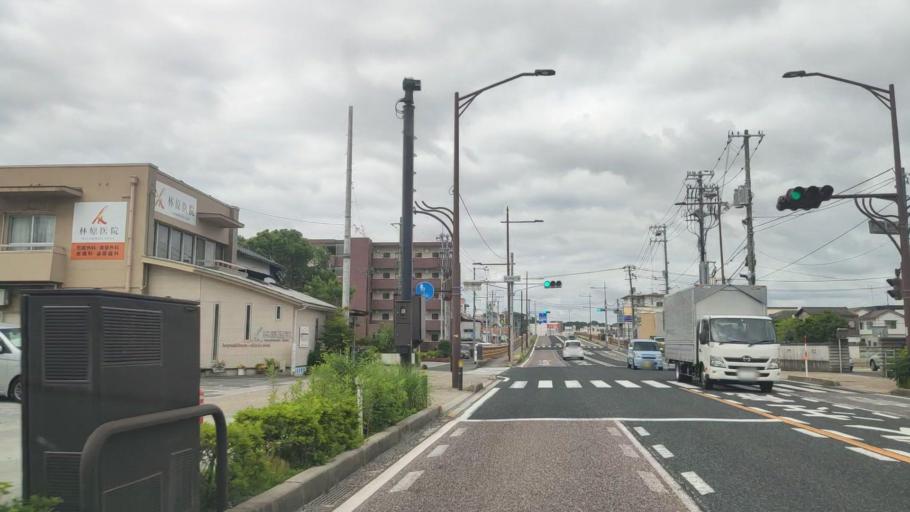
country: JP
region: Tottori
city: Yonago
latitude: 35.4366
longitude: 133.3381
